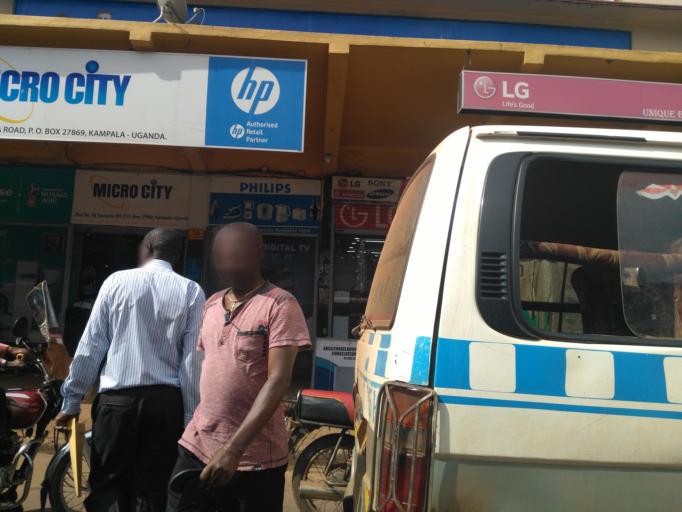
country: UG
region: Central Region
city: Kampala Central Division
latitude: 0.3177
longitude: 32.5751
